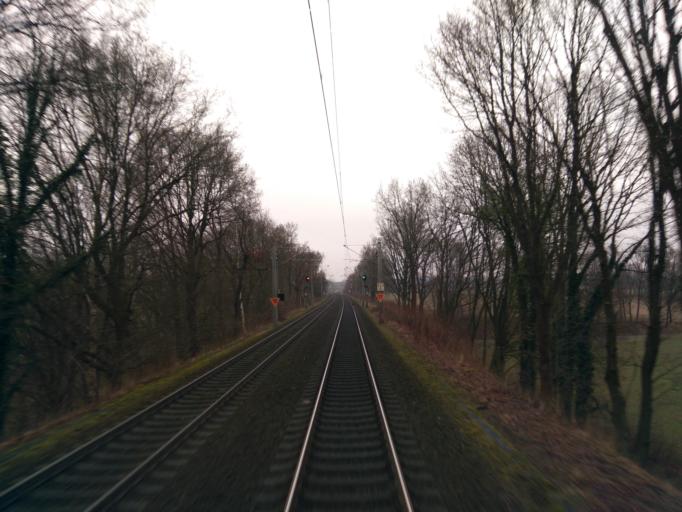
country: DE
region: Lower Saxony
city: Seevetal
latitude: 53.3963
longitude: 9.9675
